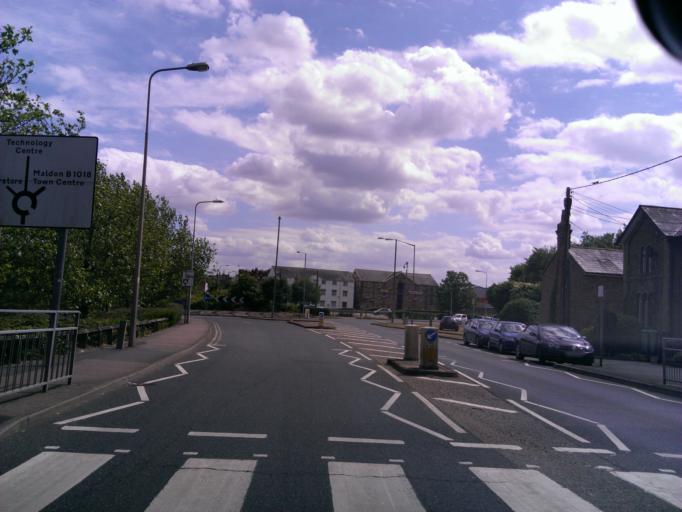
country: GB
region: England
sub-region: Essex
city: Witham
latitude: 51.8090
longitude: 0.6383
